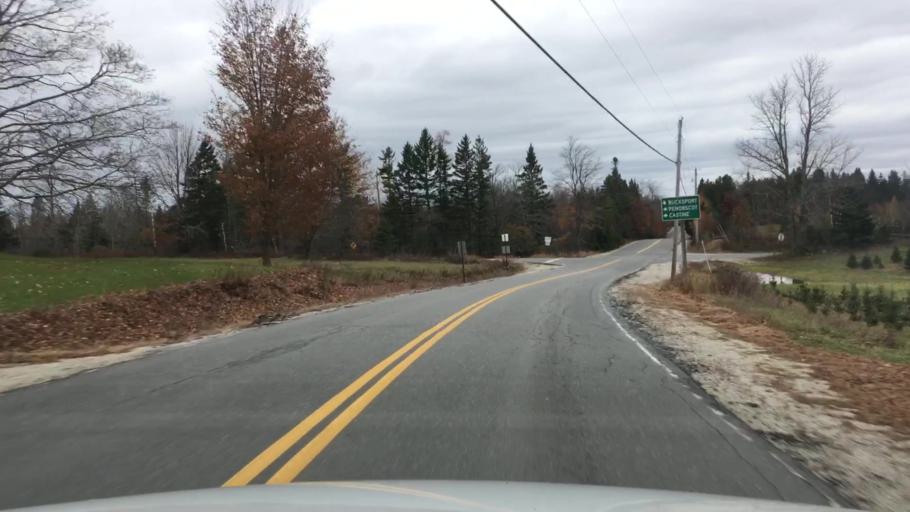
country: US
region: Maine
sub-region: Hancock County
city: Penobscot
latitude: 44.4423
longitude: -68.6363
